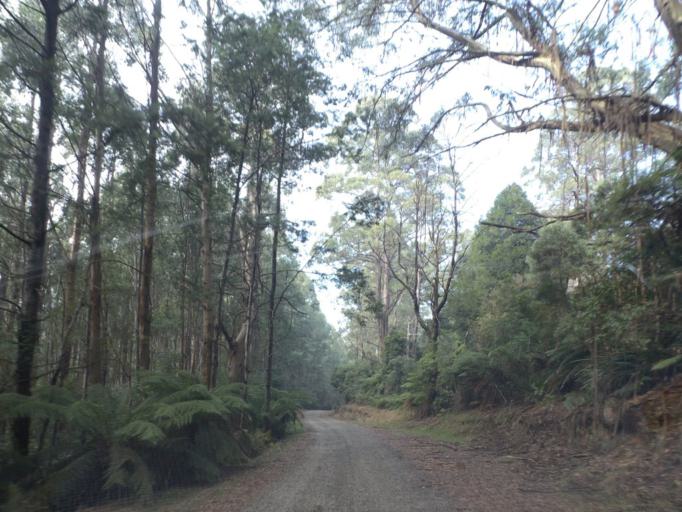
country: AU
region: Victoria
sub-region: Yarra Ranges
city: Healesville
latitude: -37.5653
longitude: 145.5408
